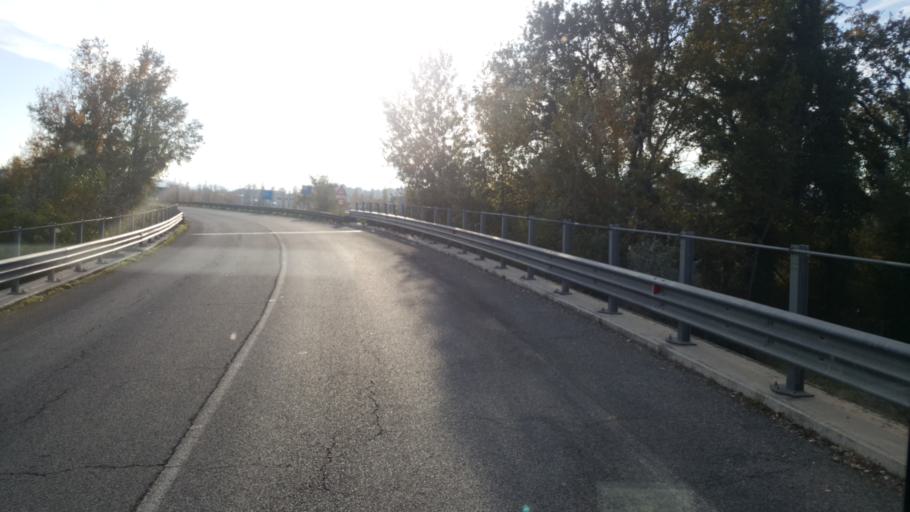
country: IT
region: The Marches
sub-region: Provincia di Ancona
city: Casine
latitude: 43.6512
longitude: 13.1487
